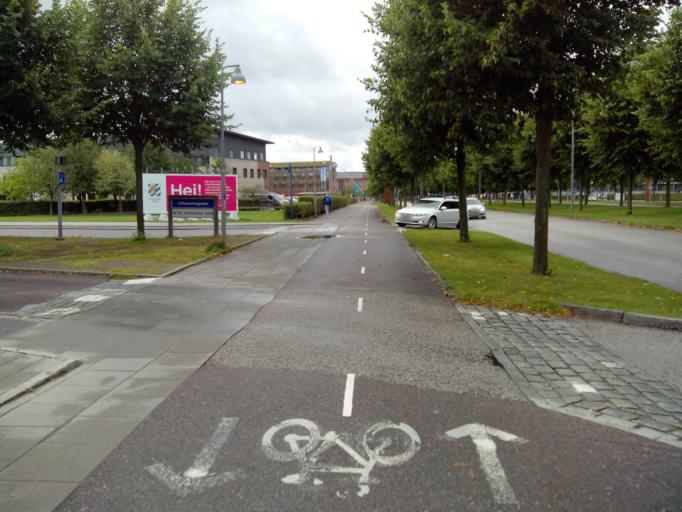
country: SE
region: Vaestra Goetaland
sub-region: Goteborg
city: Goeteborg
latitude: 57.7101
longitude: 11.9421
